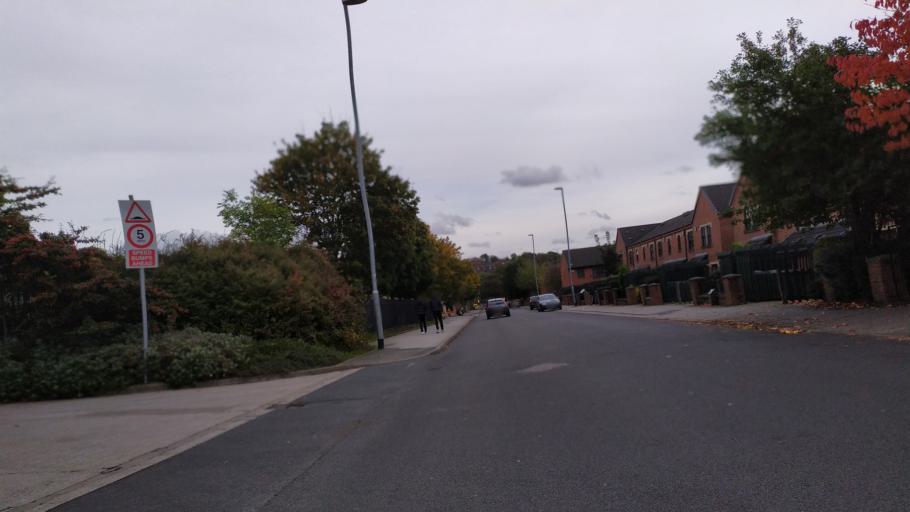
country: GB
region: England
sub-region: City and Borough of Leeds
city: Chapel Allerton
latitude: 53.8281
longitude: -1.5643
